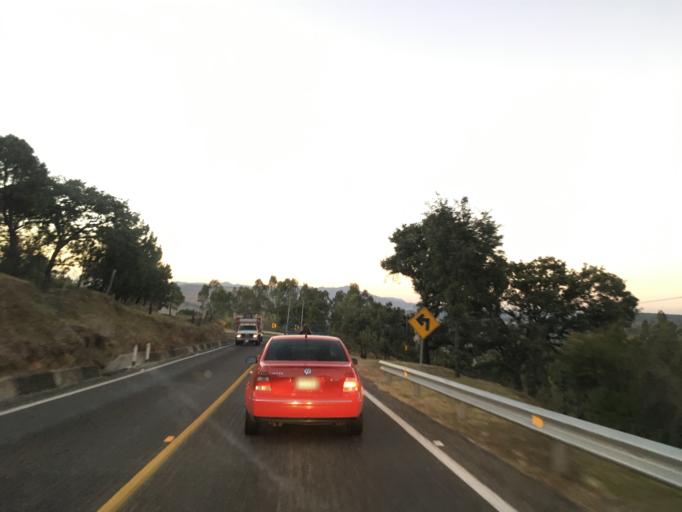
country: MX
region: Michoacan
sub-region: Zinapecuaro
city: Santa Clara del Tule
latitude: 19.8123
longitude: -100.8116
